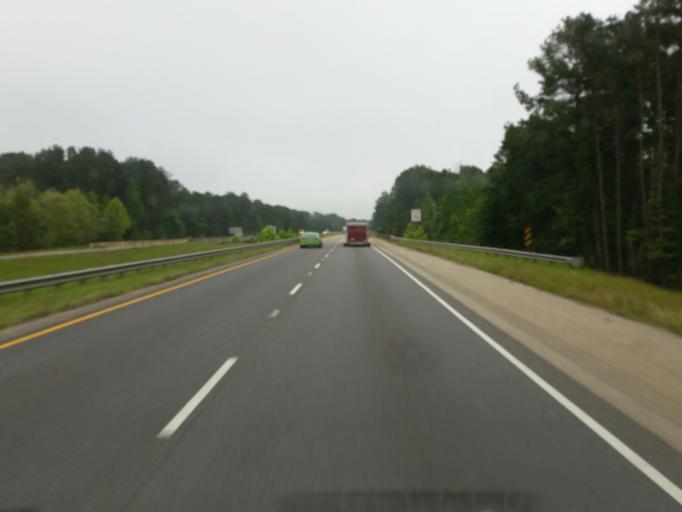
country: US
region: Louisiana
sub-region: Webster Parish
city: Minden
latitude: 32.5918
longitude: -93.3307
